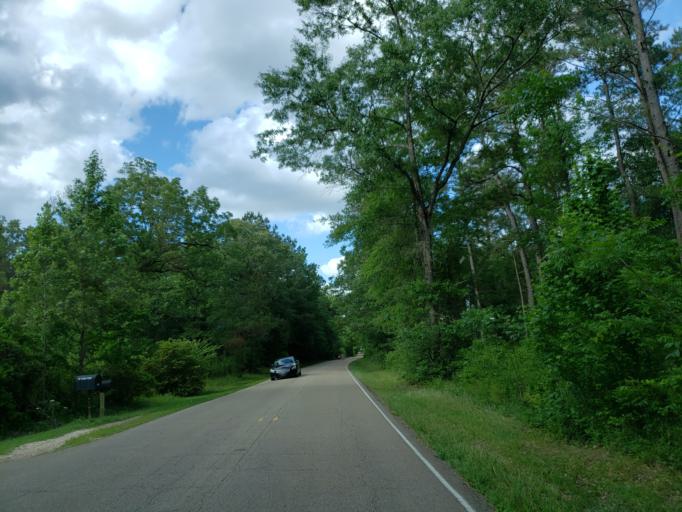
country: US
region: Mississippi
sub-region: Forrest County
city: Hattiesburg
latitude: 31.2497
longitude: -89.2412
